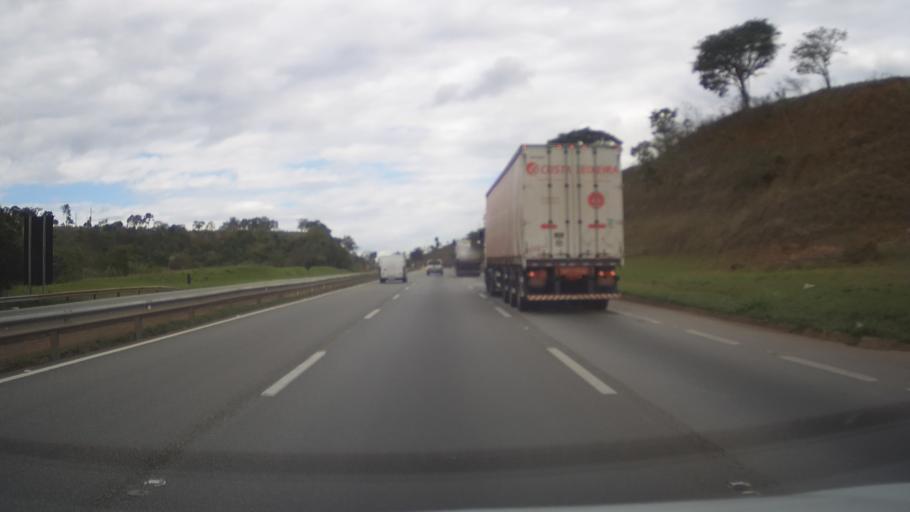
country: BR
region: Minas Gerais
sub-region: Itauna
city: Itauna
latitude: -20.3483
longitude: -44.4435
